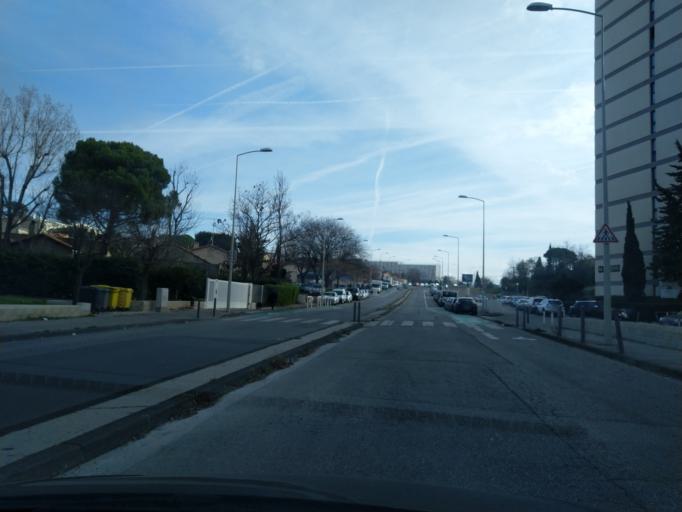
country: FR
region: Provence-Alpes-Cote d'Azur
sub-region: Departement des Bouches-du-Rhone
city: Marseille 12
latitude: 43.2985
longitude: 5.4313
